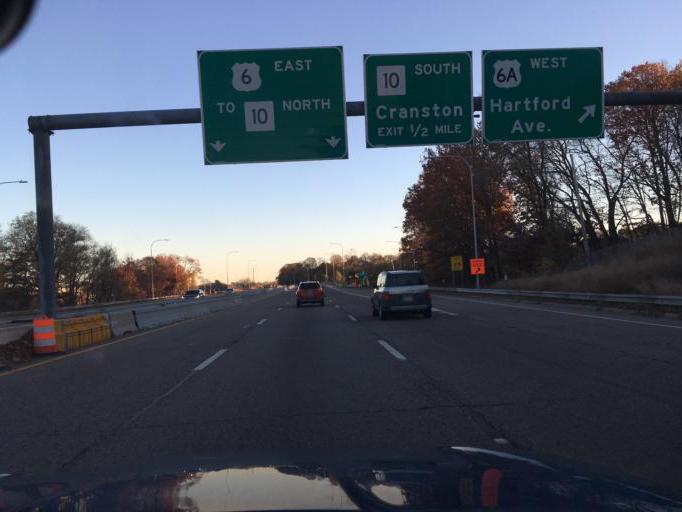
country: US
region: Rhode Island
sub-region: Providence County
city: North Providence
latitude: 41.8195
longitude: -71.4508
